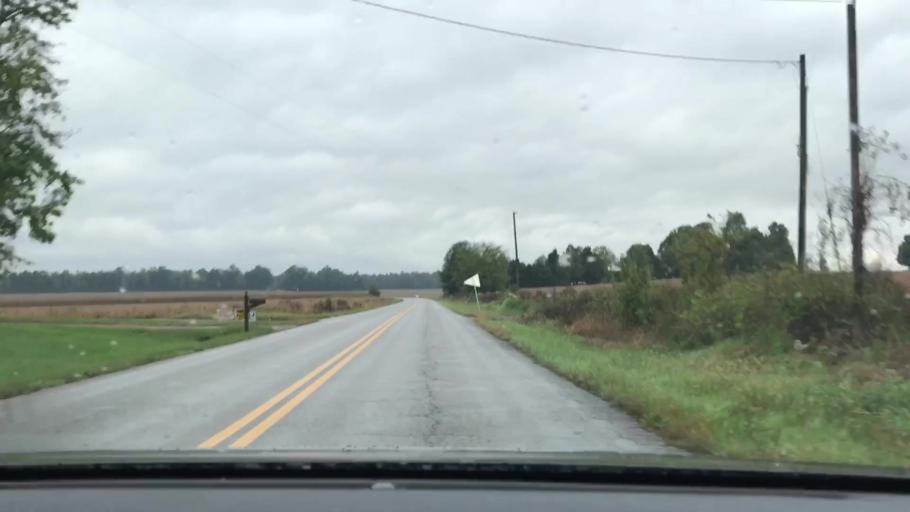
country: US
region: Kentucky
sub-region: McLean County
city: Calhoun
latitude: 37.3976
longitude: -87.2803
